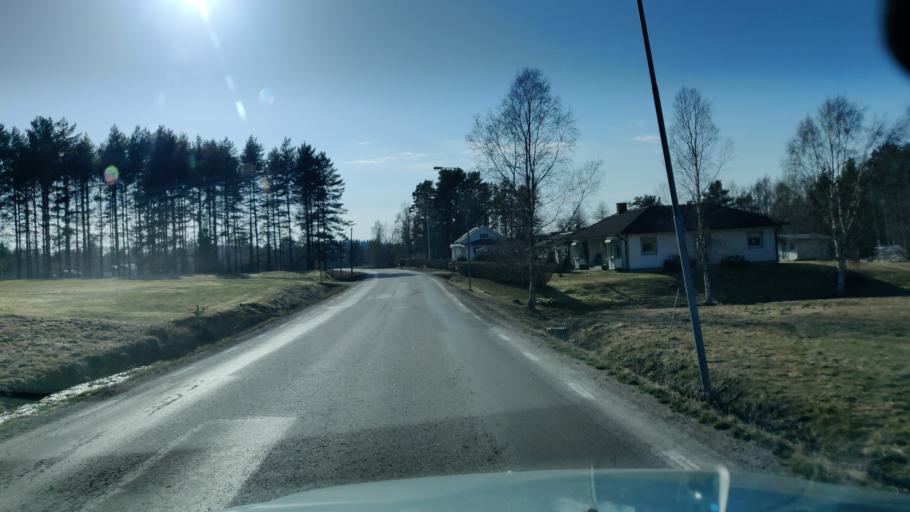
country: SE
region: Vaermland
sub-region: Sunne Kommun
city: Sunne
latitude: 59.9934
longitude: 13.2926
